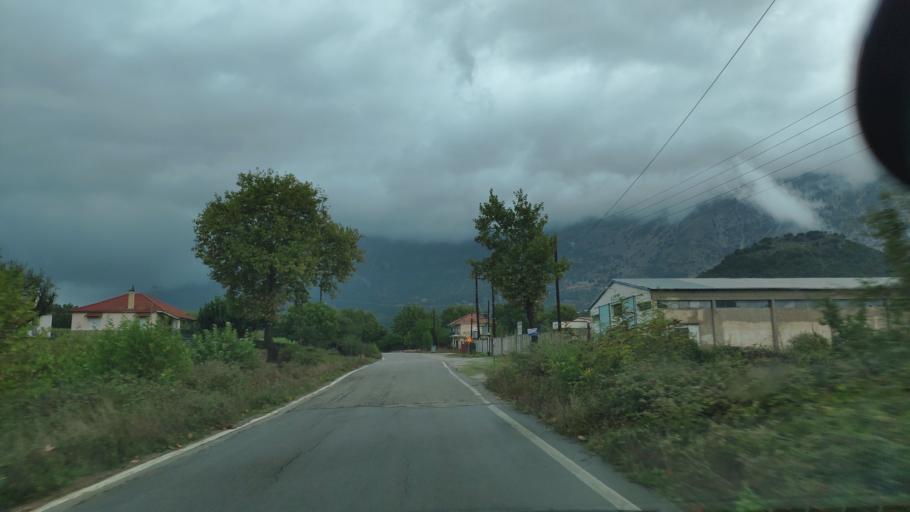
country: GR
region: West Greece
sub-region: Nomos Aitolias kai Akarnanias
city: Krikellos
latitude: 39.0089
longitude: 21.3098
